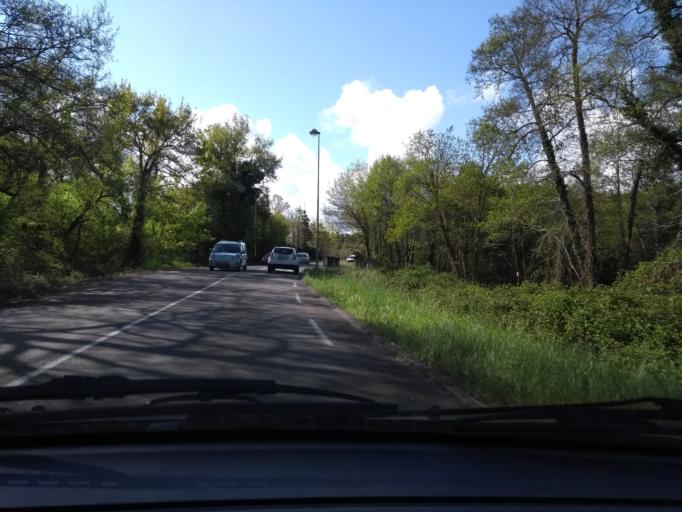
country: FR
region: Aquitaine
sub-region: Departement des Landes
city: Parentis-en-Born
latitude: 44.3419
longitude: -1.0811
